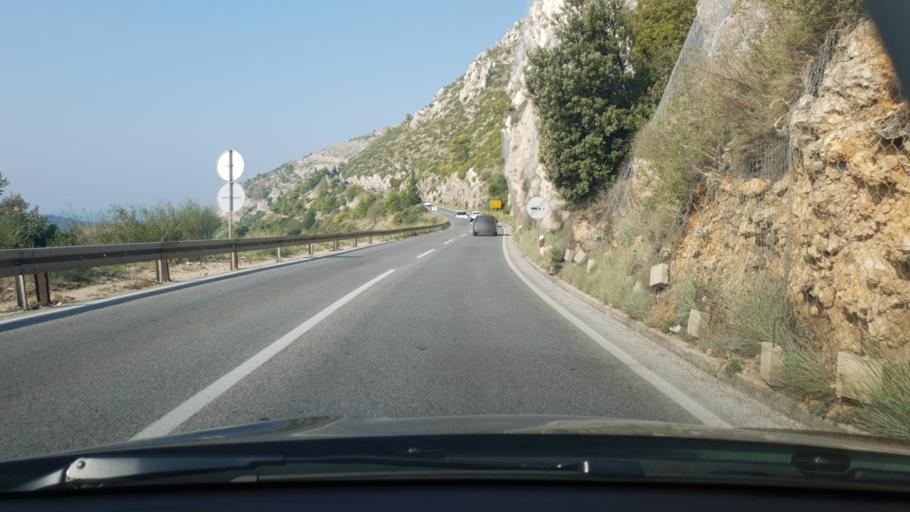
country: HR
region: Dubrovacko-Neretvanska
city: Cibaca
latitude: 42.6304
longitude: 18.1509
